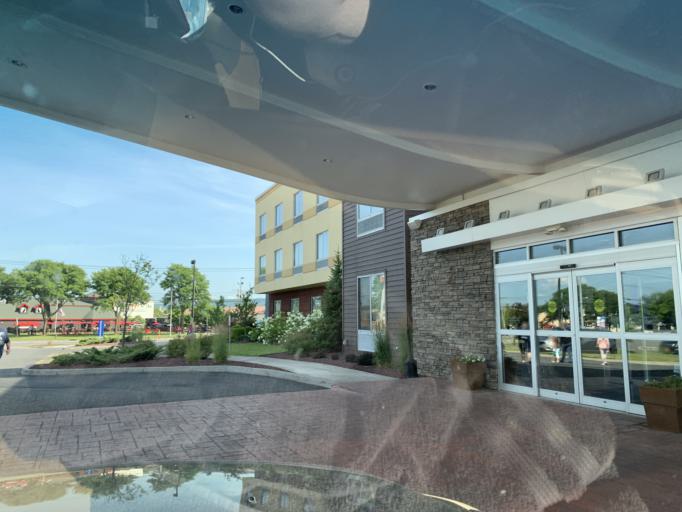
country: US
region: New York
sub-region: Oneida County
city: Utica
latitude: 43.1077
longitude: -75.2225
